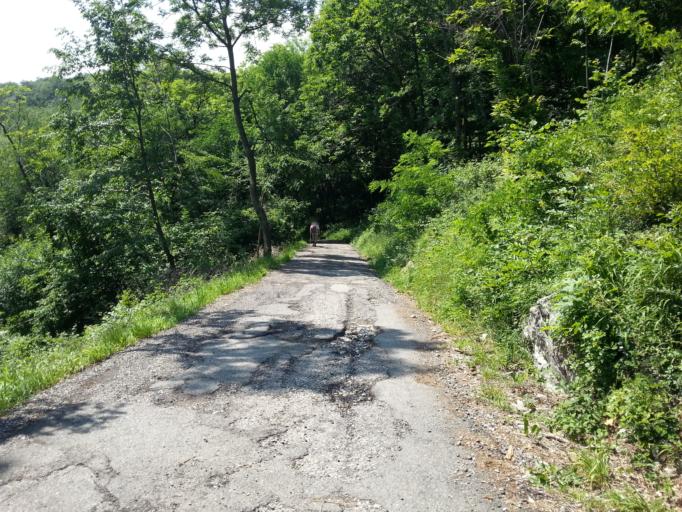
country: IT
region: Lombardy
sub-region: Provincia di Varese
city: Viggiu
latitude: 45.8804
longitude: 8.9044
